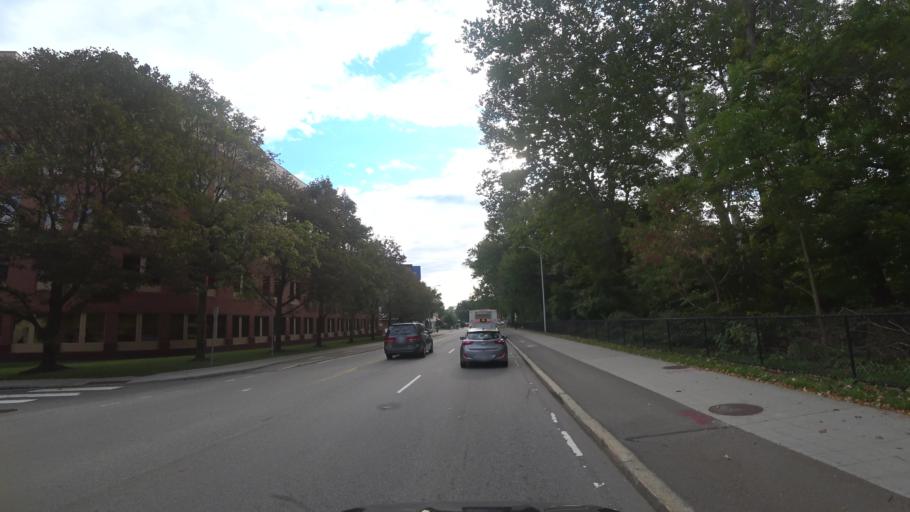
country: US
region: Massachusetts
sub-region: Middlesex County
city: Arlington
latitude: 42.3892
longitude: -71.1463
